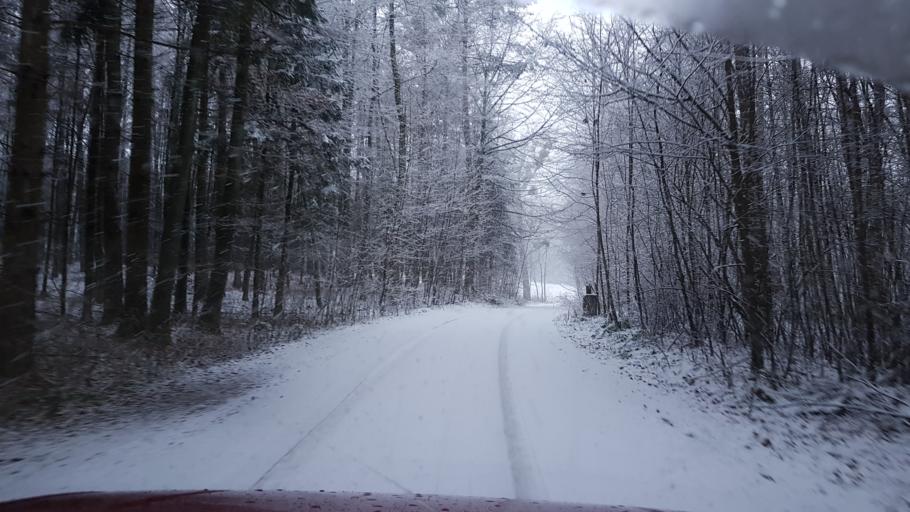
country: PL
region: West Pomeranian Voivodeship
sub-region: Powiat koszalinski
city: Polanow
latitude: 54.2379
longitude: 16.6530
